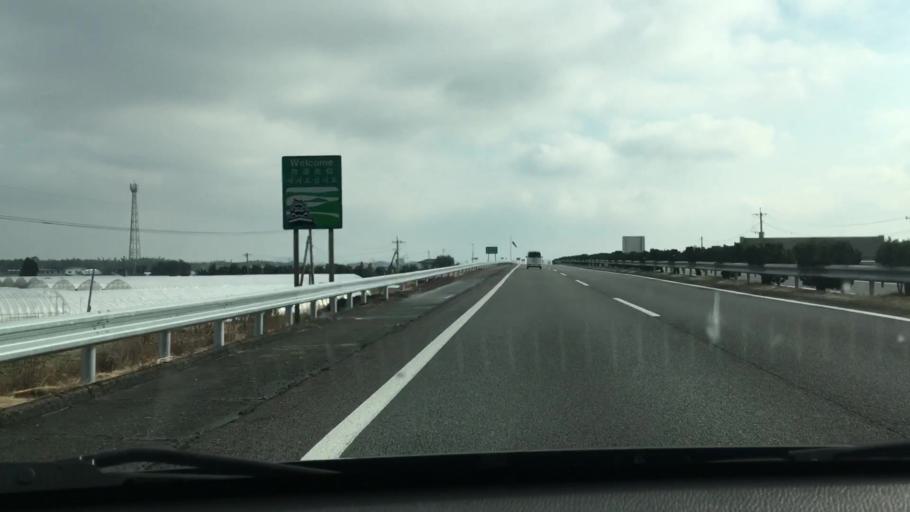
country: JP
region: Kumamoto
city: Ueki
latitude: 32.8899
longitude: 130.7221
